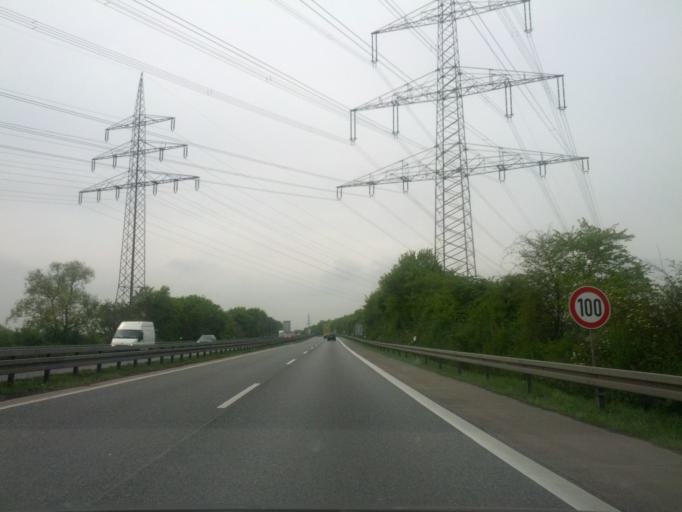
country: DE
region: Hesse
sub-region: Regierungsbezirk Giessen
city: Heuchelheim
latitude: 50.5791
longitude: 8.6487
